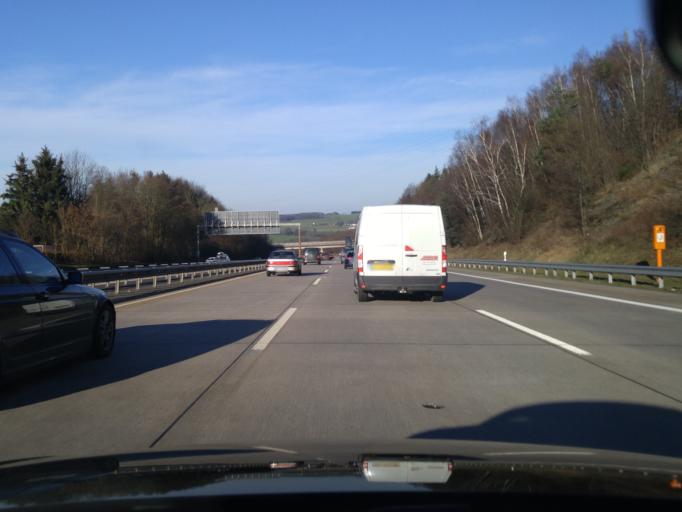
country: DE
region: Rheinland-Pfalz
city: Breitscheid
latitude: 50.6083
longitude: 7.4281
